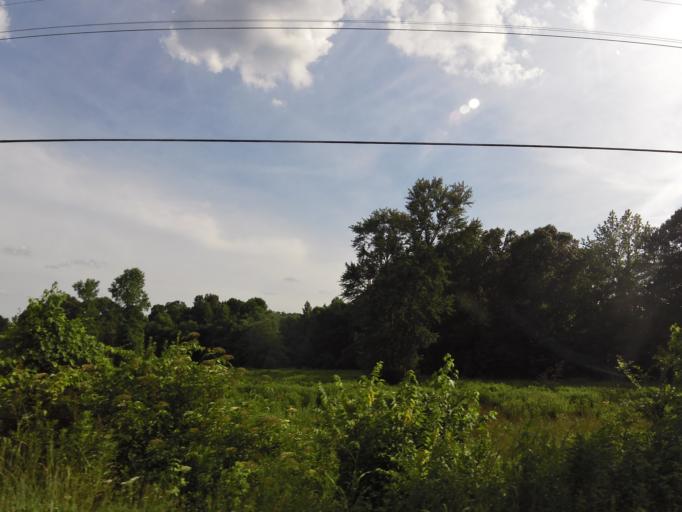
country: US
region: Tennessee
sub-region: Benton County
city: Camden
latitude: 36.0159
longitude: -88.0549
